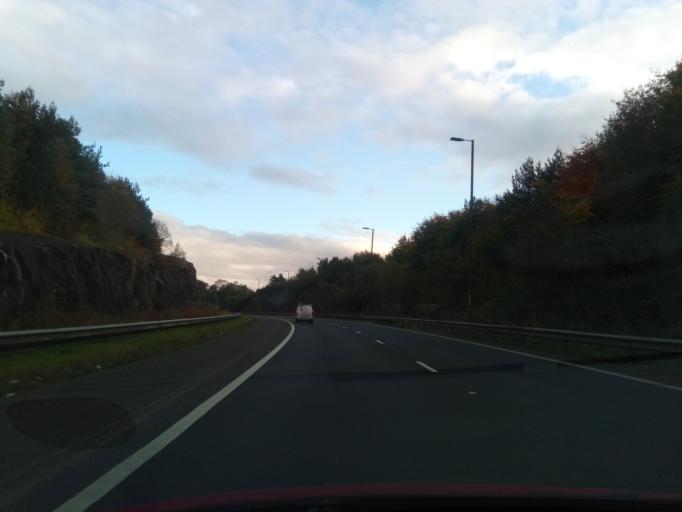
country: GB
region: Scotland
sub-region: Edinburgh
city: Newbridge
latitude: 55.9276
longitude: -3.3996
